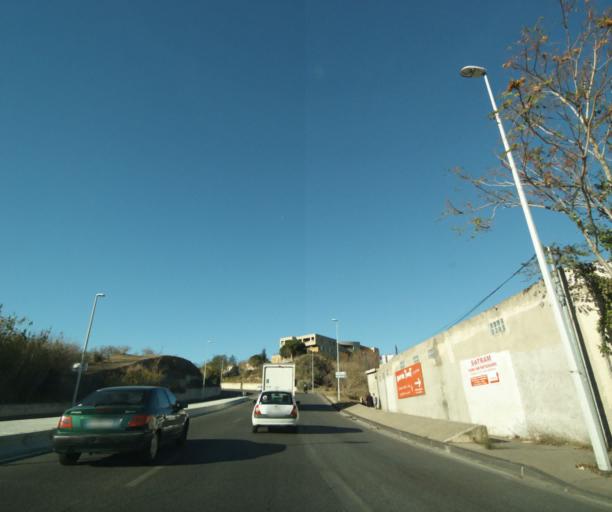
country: FR
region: Provence-Alpes-Cote d'Azur
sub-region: Departement des Bouches-du-Rhone
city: Marseille 14
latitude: 43.3486
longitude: 5.3621
